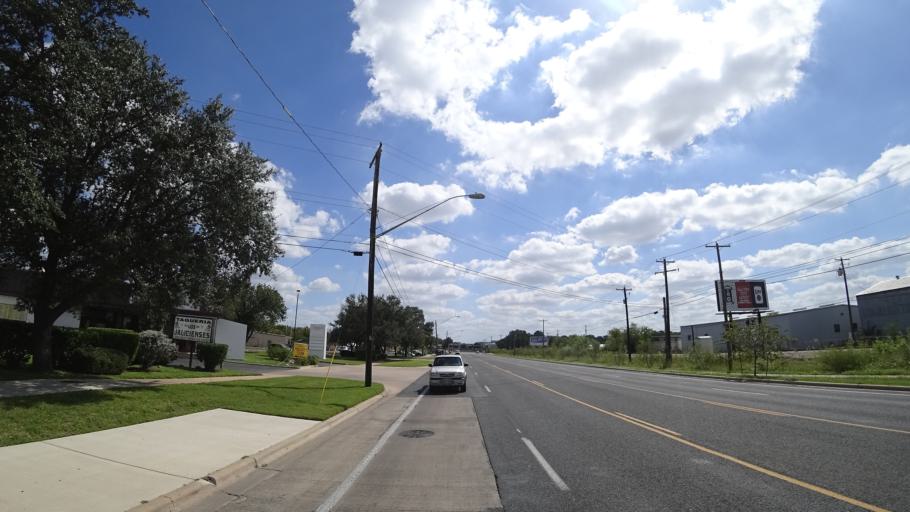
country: US
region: Texas
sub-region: Travis County
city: Austin
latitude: 30.3361
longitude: -97.7180
